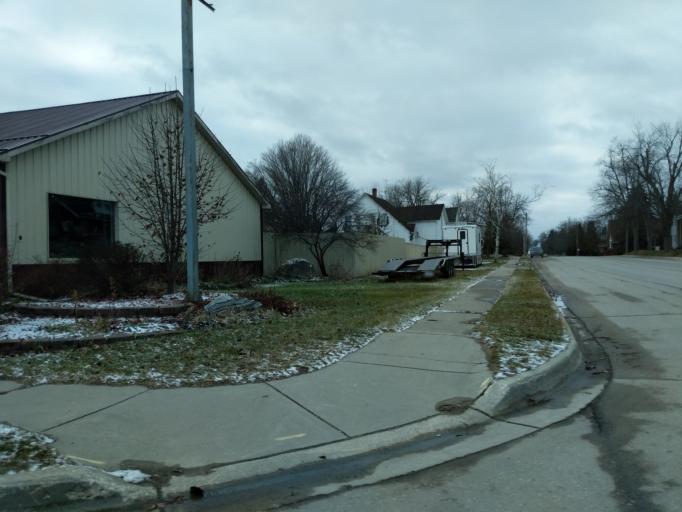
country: US
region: Michigan
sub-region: Sanilac County
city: Marlette
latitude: 43.3278
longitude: -83.0812
